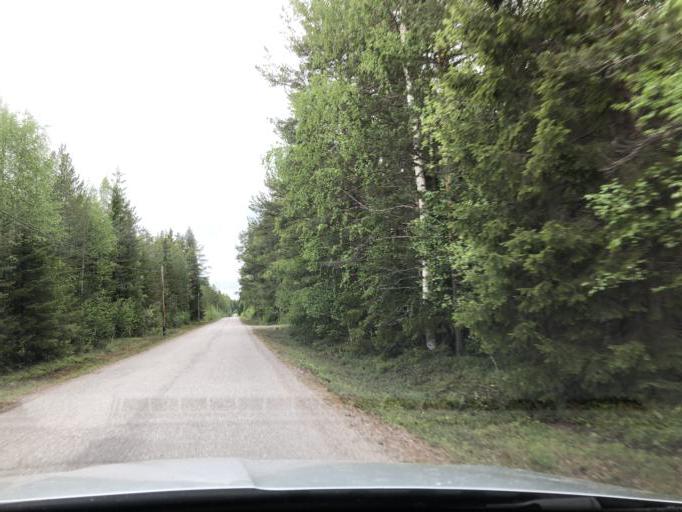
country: SE
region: Norrbotten
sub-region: Pitea Kommun
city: Roknas
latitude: 65.3800
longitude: 21.2748
